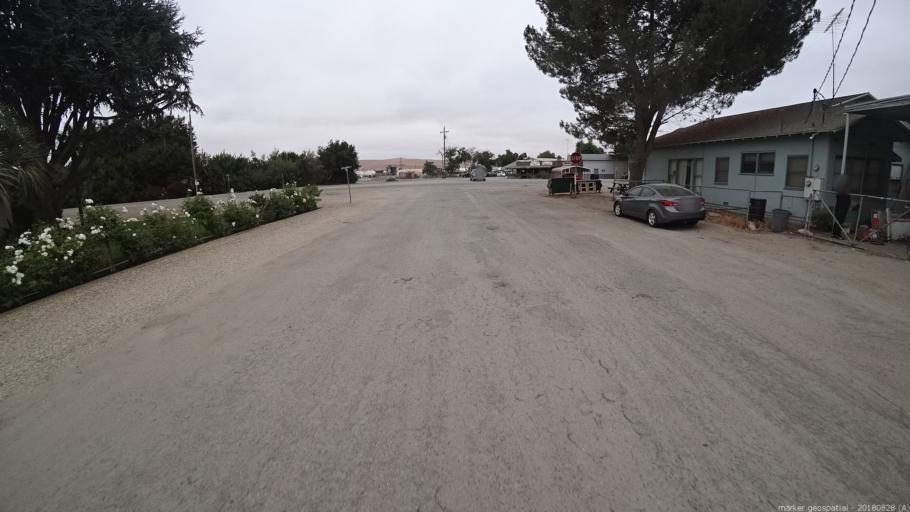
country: US
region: California
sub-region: Monterey County
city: King City
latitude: 36.0229
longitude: -120.9046
